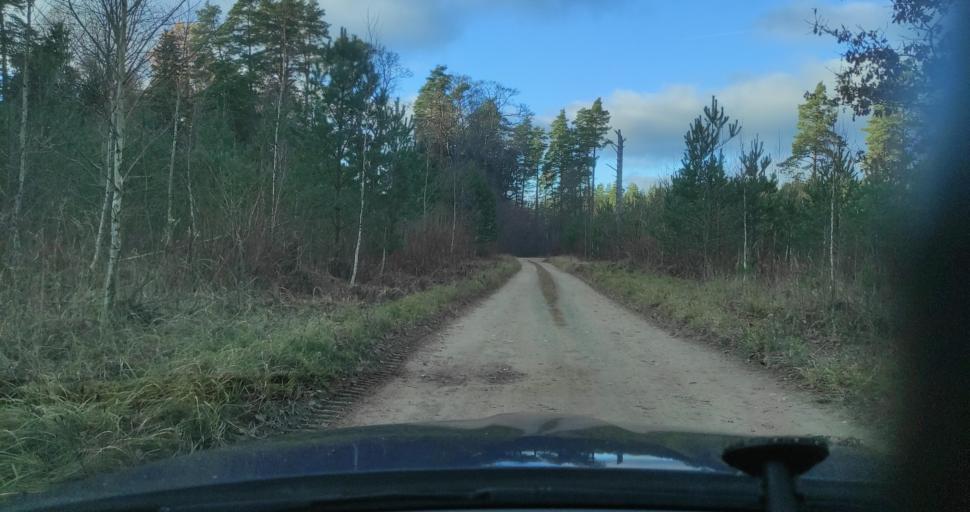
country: LV
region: Kuldigas Rajons
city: Kuldiga
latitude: 57.2814
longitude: 22.0418
